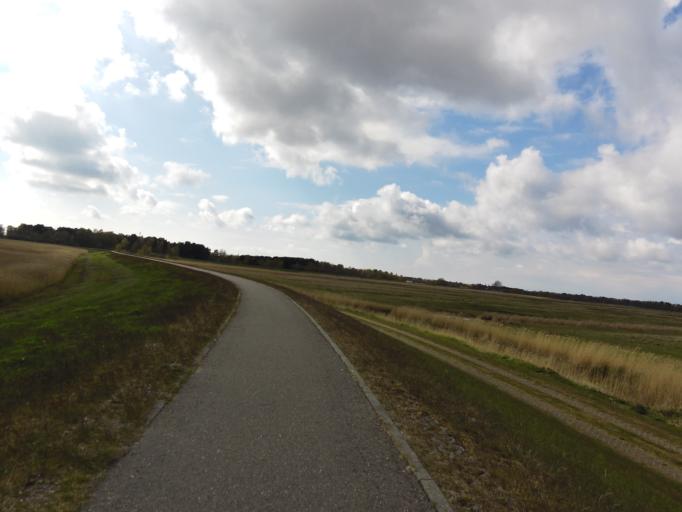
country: DE
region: Mecklenburg-Vorpommern
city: Zingst
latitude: 54.4333
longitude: 12.7246
